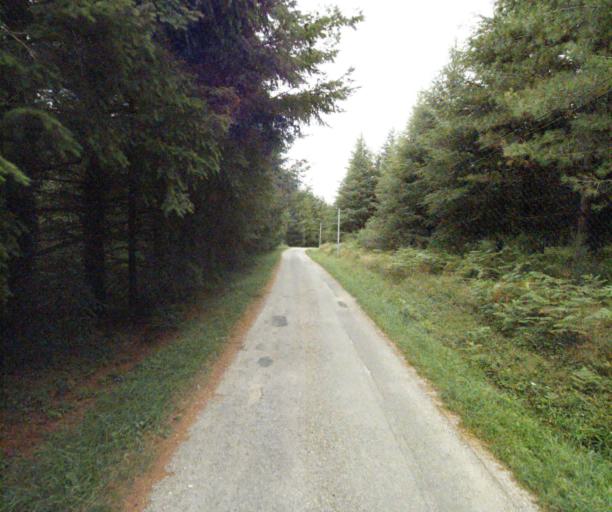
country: FR
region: Midi-Pyrenees
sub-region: Departement du Tarn
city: Soreze
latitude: 43.4181
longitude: 2.0474
